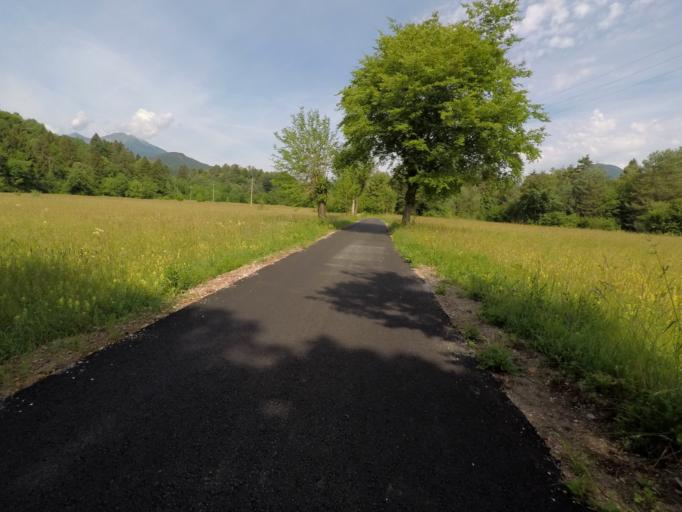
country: IT
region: Friuli Venezia Giulia
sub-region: Provincia di Udine
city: Cavazzo Carnico
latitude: 46.3615
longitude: 13.0524
